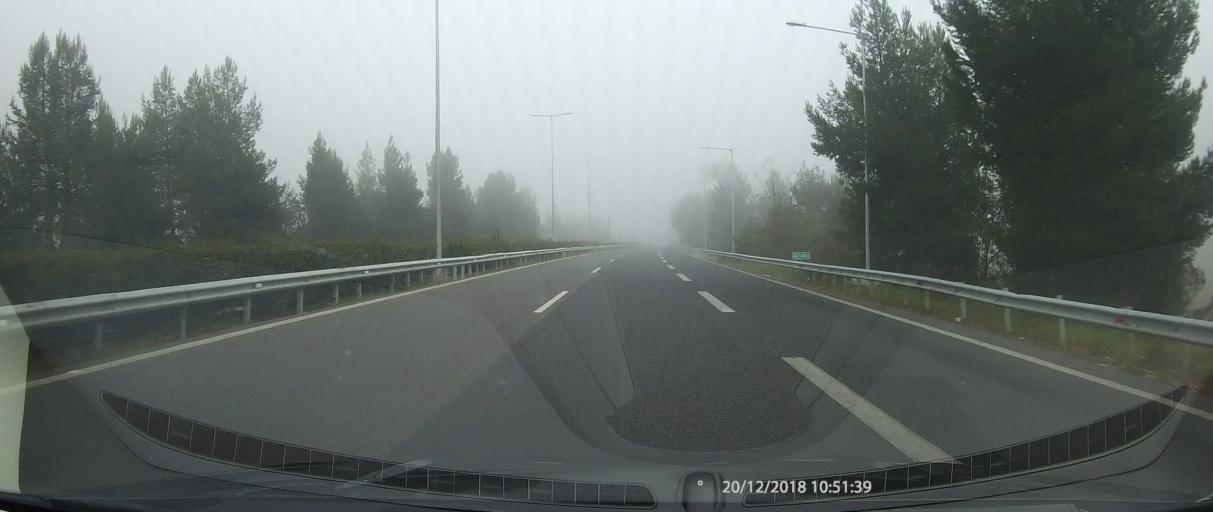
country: GR
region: Peloponnese
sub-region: Nomos Arkadias
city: Tripoli
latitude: 37.5912
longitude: 22.4373
